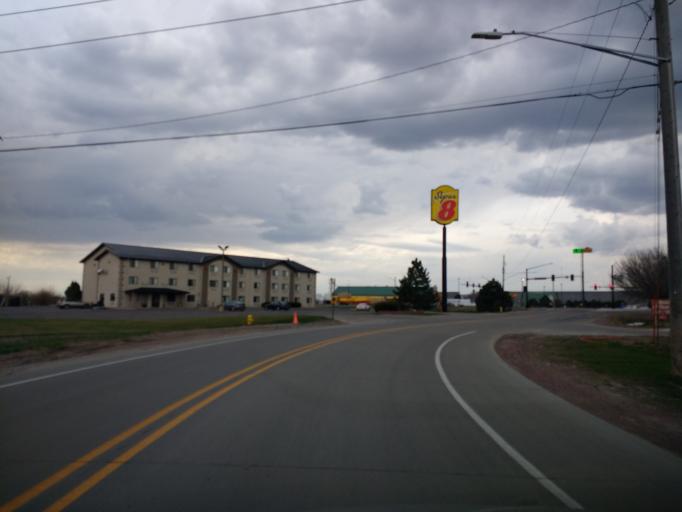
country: US
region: Iowa
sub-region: Woodbury County
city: Sergeant Bluff
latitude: 42.4328
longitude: -96.3782
